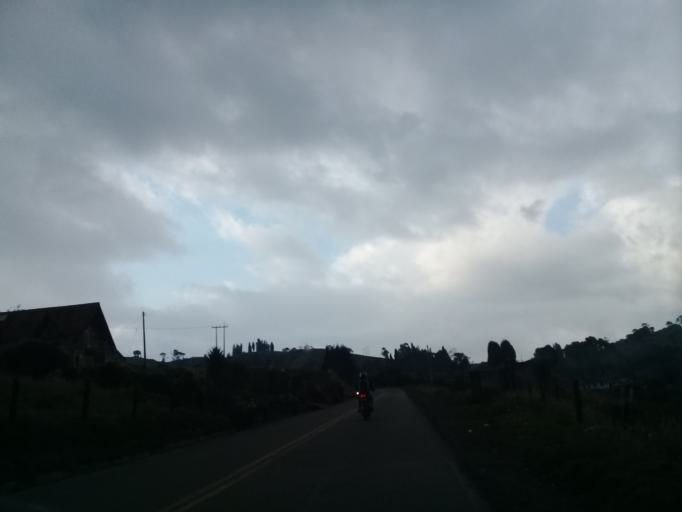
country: CO
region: Cundinamarca
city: Zipaquira
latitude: 5.0824
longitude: -74.0582
